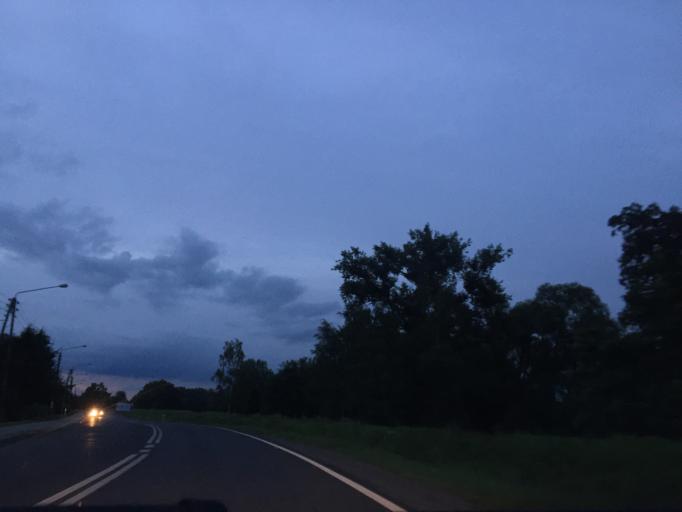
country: PL
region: Lesser Poland Voivodeship
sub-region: Powiat oswiecimski
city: Oswiecim
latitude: 50.0293
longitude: 19.2093
